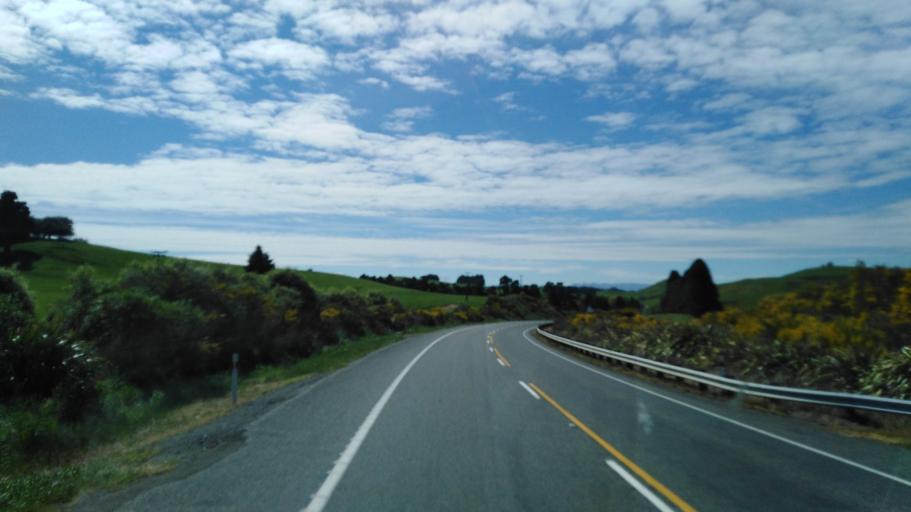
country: NZ
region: Manawatu-Wanganui
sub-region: Ruapehu District
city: Waiouru
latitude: -39.5819
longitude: 175.7309
